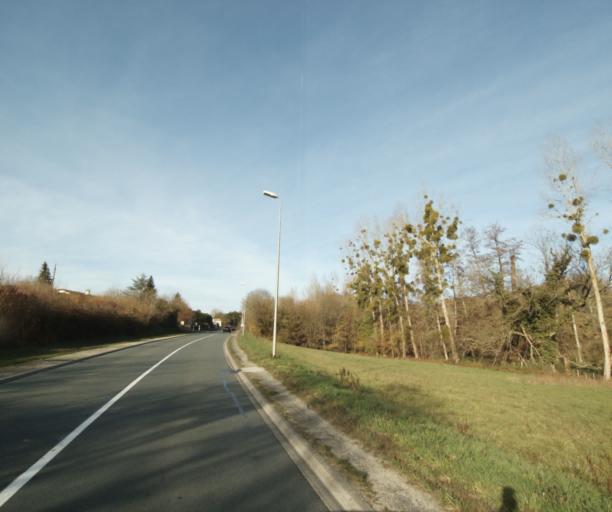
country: FR
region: Poitou-Charentes
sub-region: Departement de la Charente-Maritime
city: Chaniers
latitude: 45.7335
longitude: -0.5375
